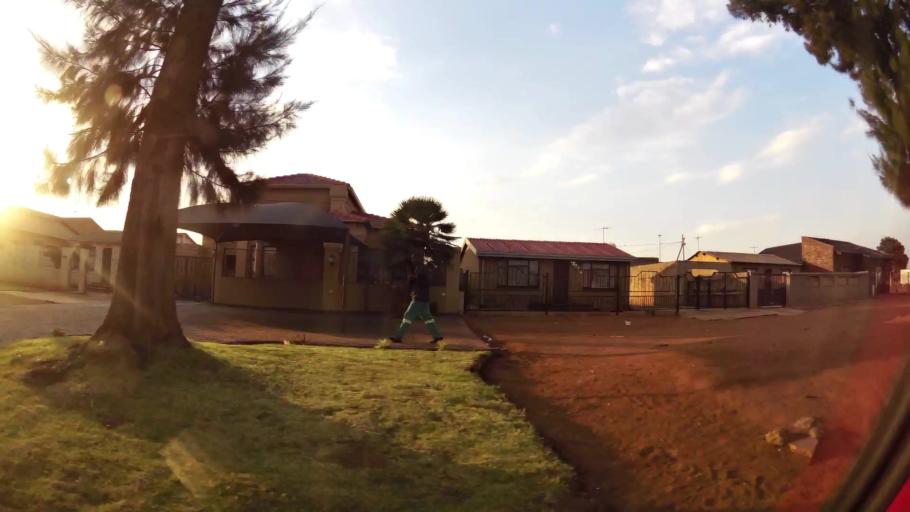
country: ZA
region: Gauteng
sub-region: City of Johannesburg Metropolitan Municipality
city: Orange Farm
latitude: -26.5937
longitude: 27.8292
